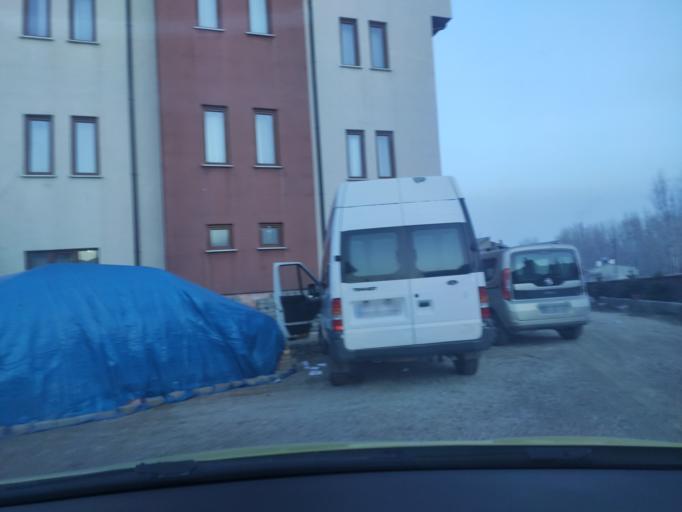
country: TR
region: Bayburt
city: Aydintepe
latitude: 40.3890
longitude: 40.1538
